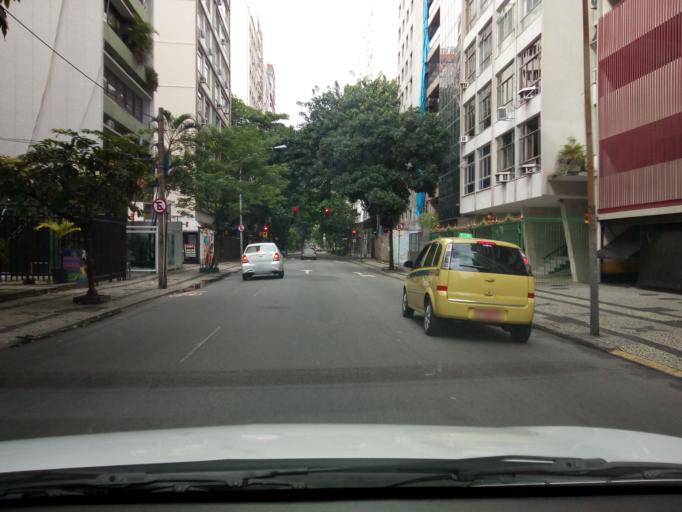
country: BR
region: Rio de Janeiro
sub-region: Rio De Janeiro
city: Rio de Janeiro
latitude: -22.9653
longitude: -43.1826
